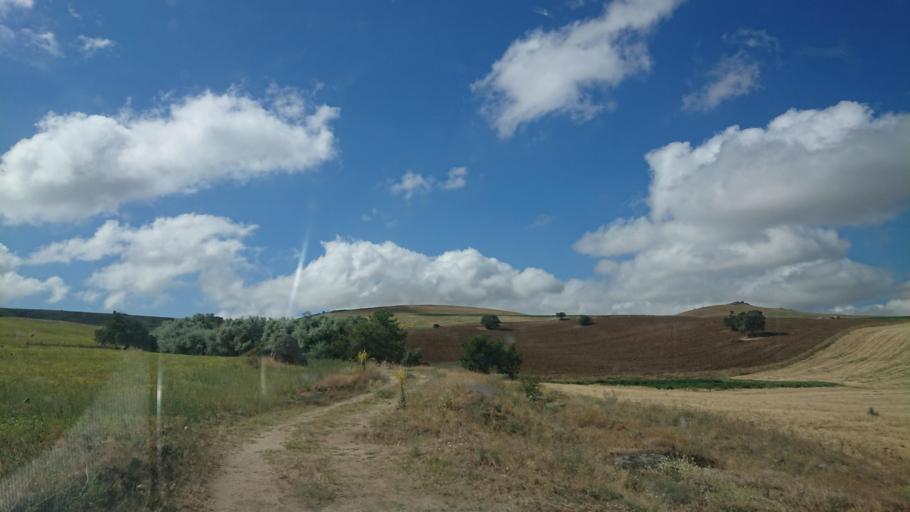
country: TR
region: Aksaray
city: Agacoren
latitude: 38.8436
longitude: 33.9366
